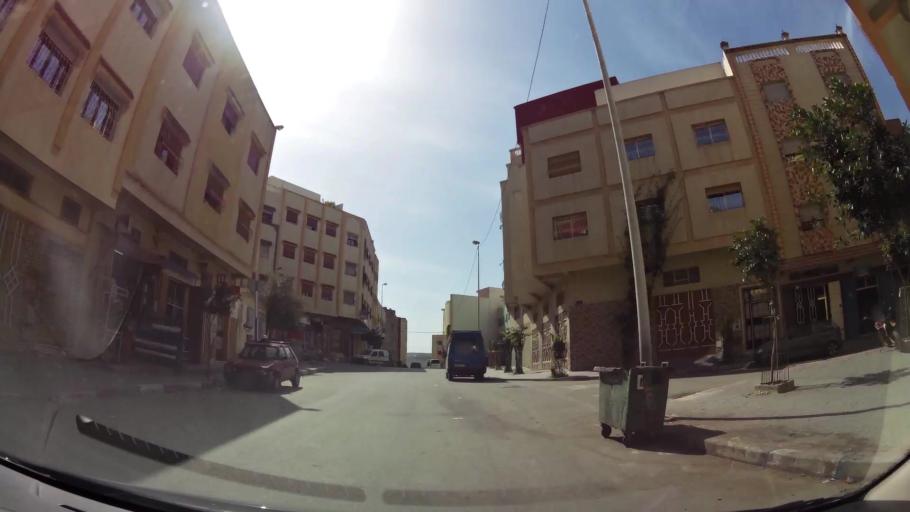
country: MA
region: Tanger-Tetouan
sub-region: Tanger-Assilah
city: Tangier
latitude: 35.7341
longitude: -5.8033
